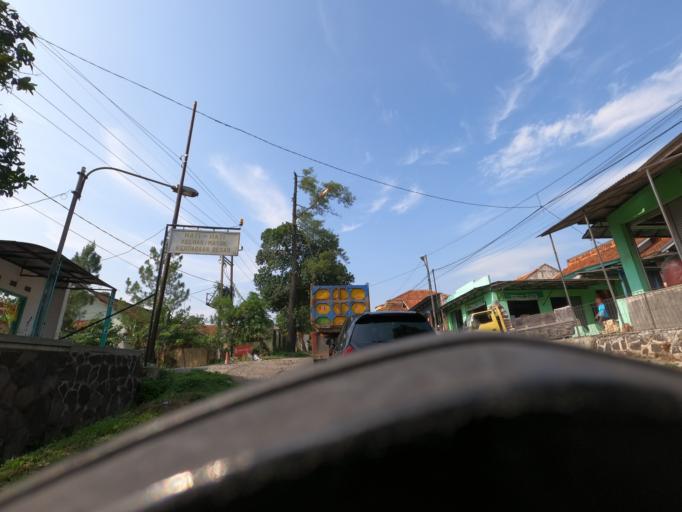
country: ID
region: West Java
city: Lembang
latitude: -6.6478
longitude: 107.7217
